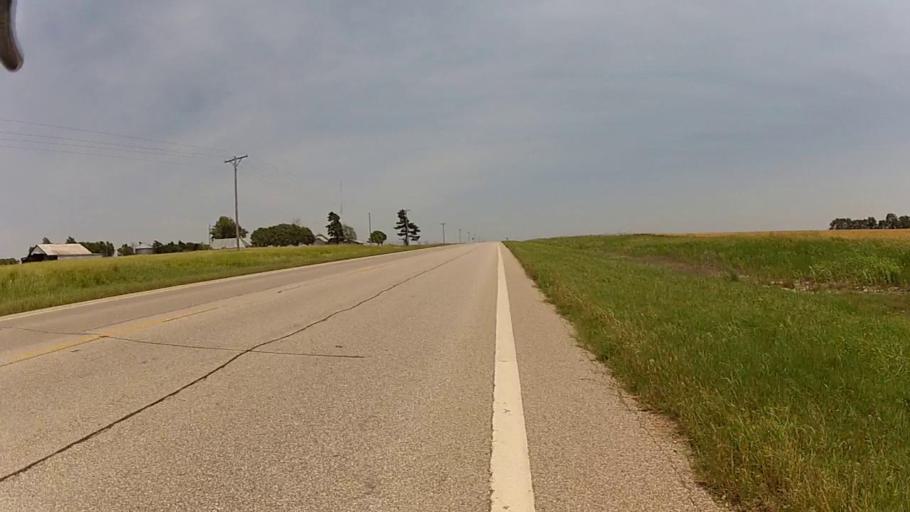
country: US
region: Kansas
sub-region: Cowley County
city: Arkansas City
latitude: 37.0565
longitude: -97.1053
